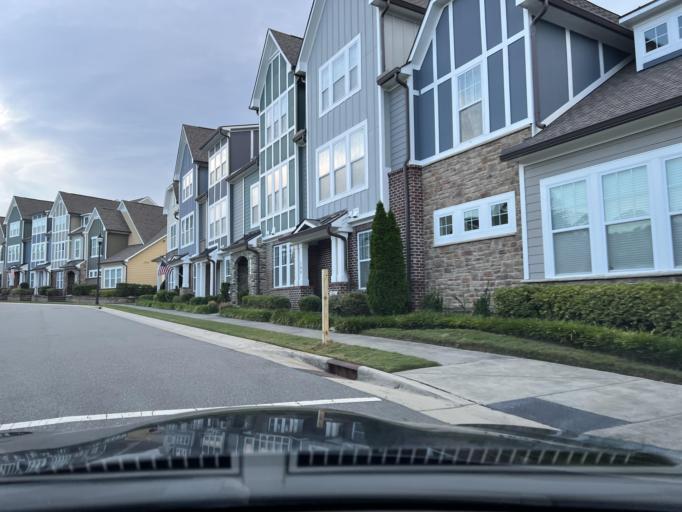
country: US
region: North Carolina
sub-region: Wake County
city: Raleigh
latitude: 35.8138
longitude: -78.6311
